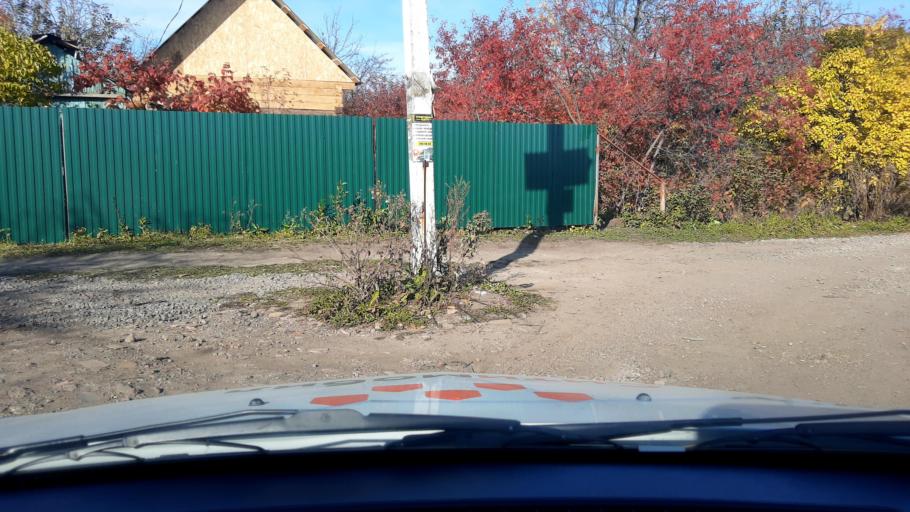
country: RU
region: Bashkortostan
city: Ufa
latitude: 54.8282
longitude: 56.1013
